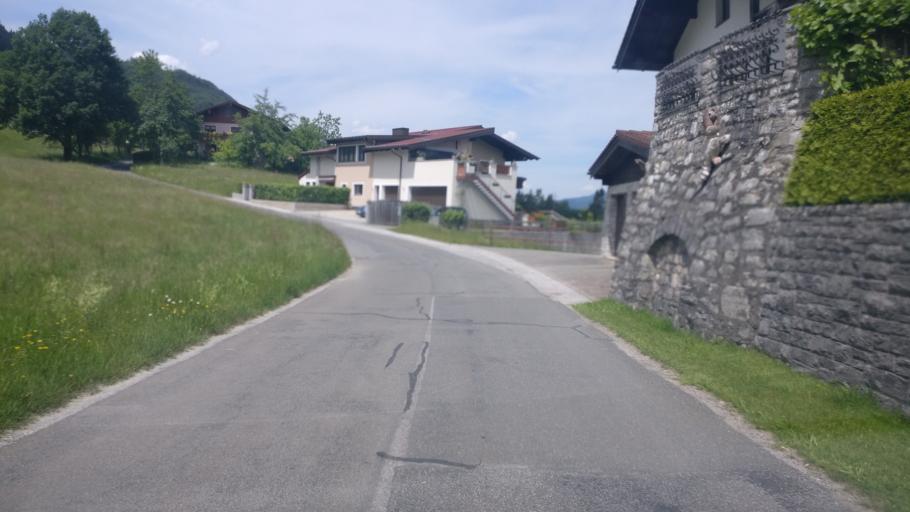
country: AT
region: Salzburg
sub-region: Politischer Bezirk Hallein
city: Kuchl
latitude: 47.6333
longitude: 13.1302
